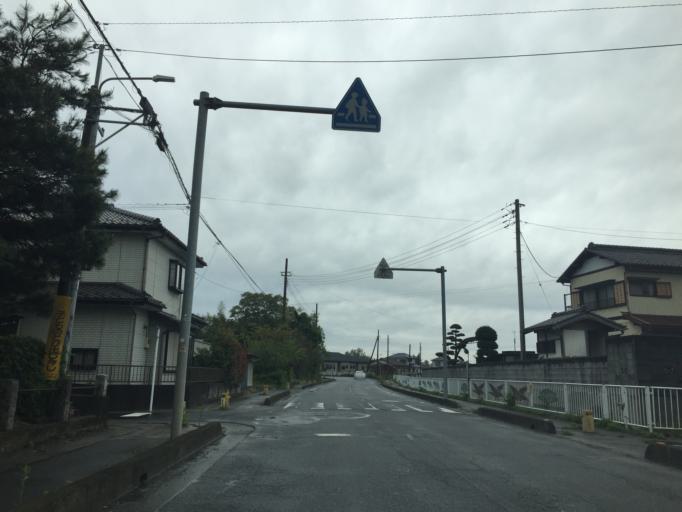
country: JP
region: Saitama
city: Shiki
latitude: 35.8622
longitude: 139.5697
